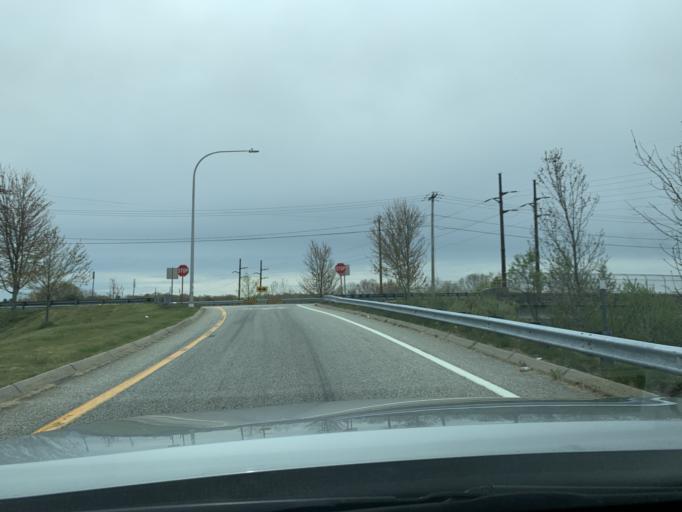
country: US
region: Rhode Island
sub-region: Kent County
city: East Greenwich
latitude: 41.6086
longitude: -71.4727
